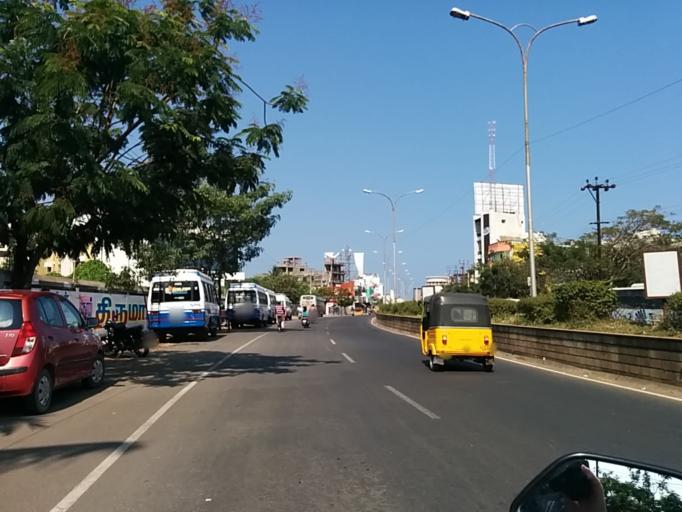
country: IN
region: Pondicherry
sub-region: Puducherry
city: Puducherry
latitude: 11.9507
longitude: 79.8155
